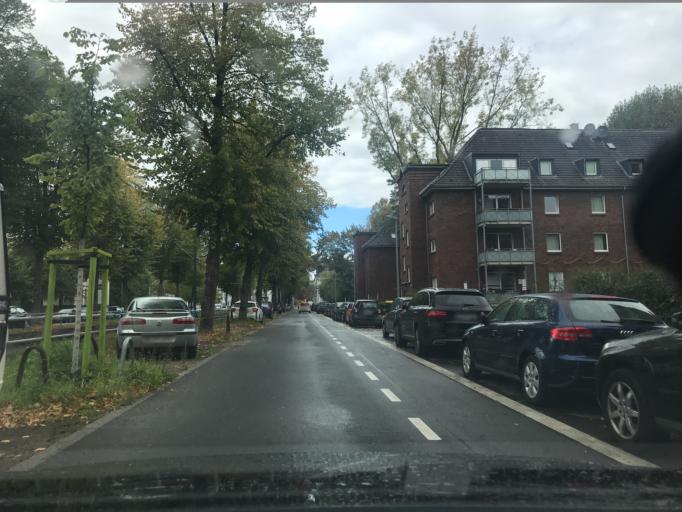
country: DE
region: North Rhine-Westphalia
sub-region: Regierungsbezirk Dusseldorf
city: Dusseldorf
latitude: 51.2411
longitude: 6.7258
